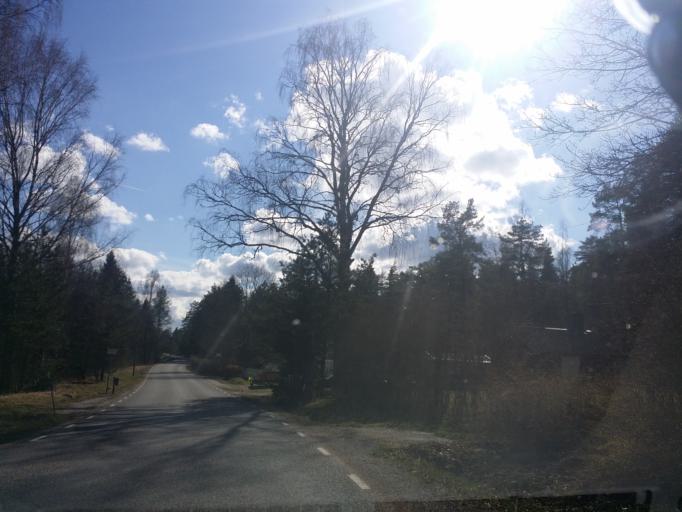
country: SE
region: Vaestmanland
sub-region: Sala Kommun
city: Sala
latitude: 59.9964
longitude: 16.4872
